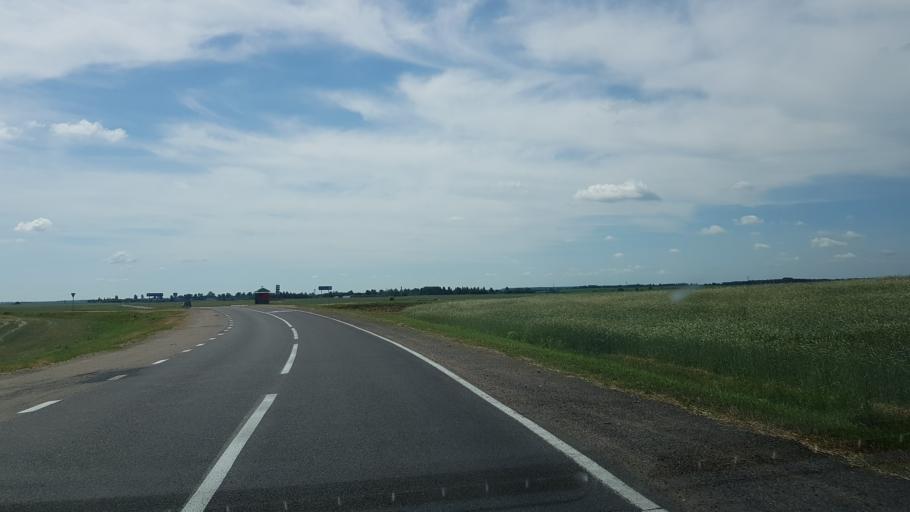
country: BY
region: Vitebsk
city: Dubrowna
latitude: 54.6315
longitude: 30.6638
